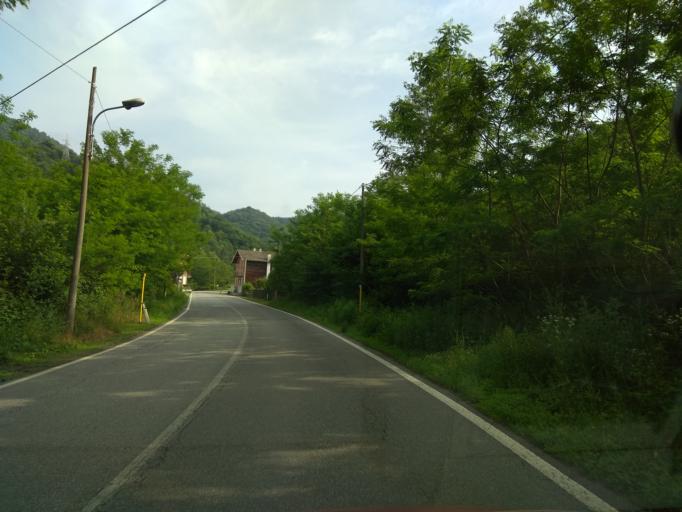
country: IT
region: Piedmont
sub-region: Provincia di Biella
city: Pray
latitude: 45.6696
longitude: 8.2125
